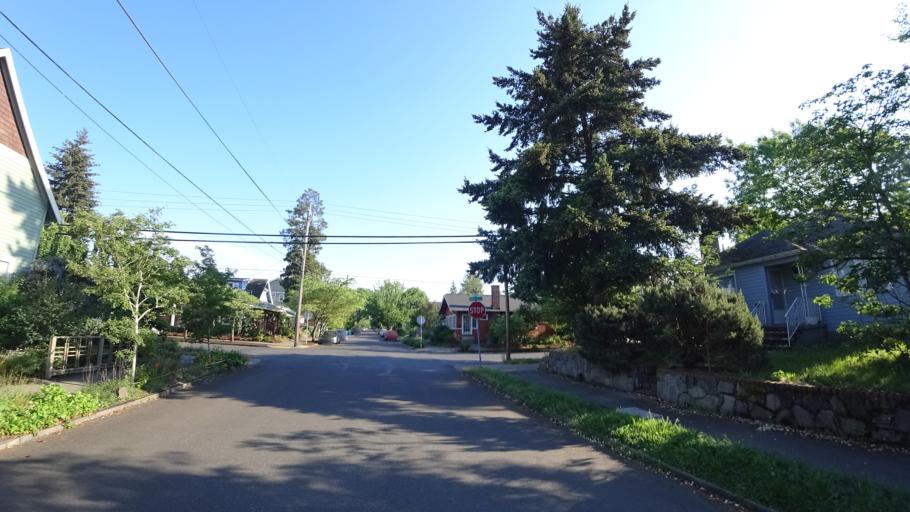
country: US
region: Oregon
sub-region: Multnomah County
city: Portland
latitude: 45.5566
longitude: -122.6389
